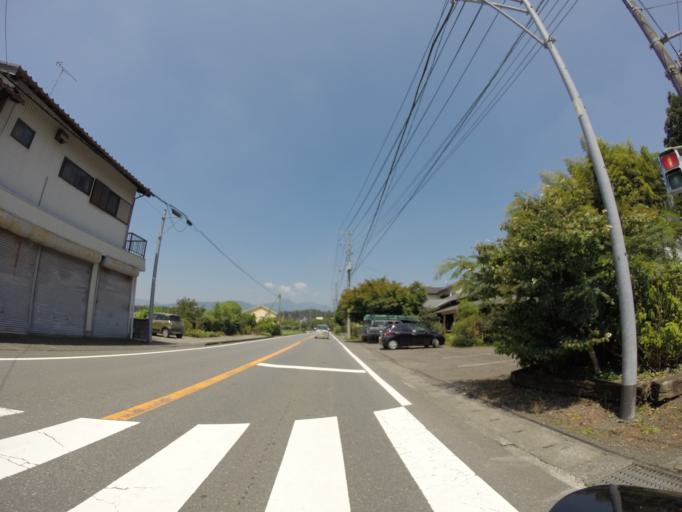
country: JP
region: Shizuoka
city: Fujinomiya
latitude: 35.2710
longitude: 138.6193
